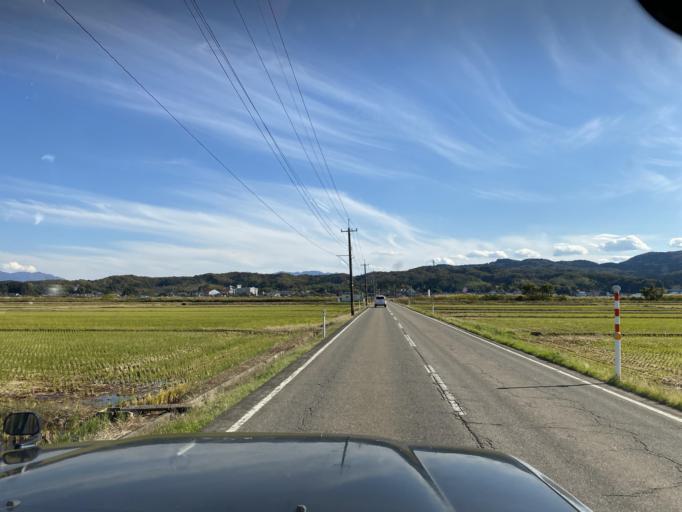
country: JP
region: Niigata
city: Niitsu-honcho
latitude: 37.7575
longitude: 139.0892
